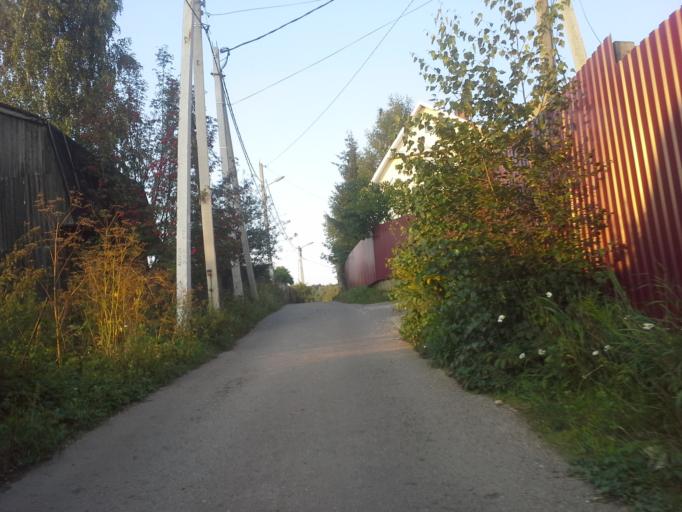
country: RU
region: Moskovskaya
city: Kommunarka
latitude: 55.5081
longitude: 37.4391
